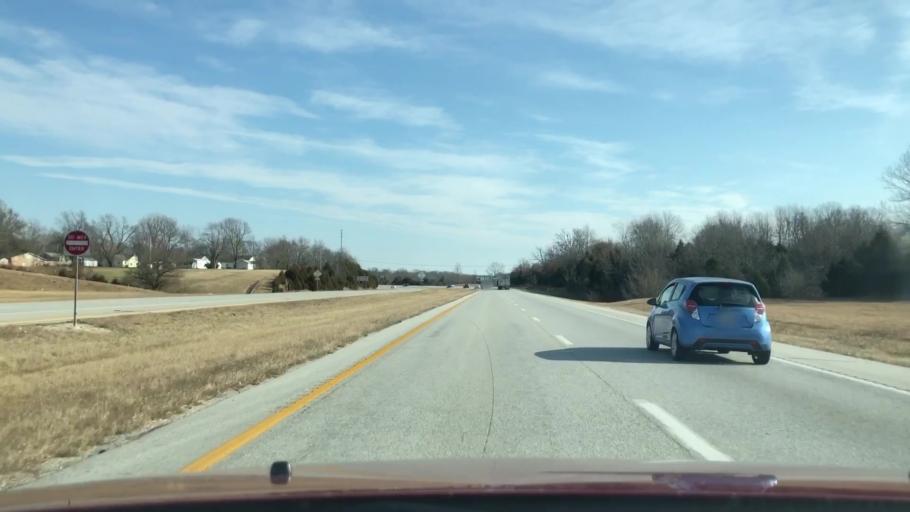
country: US
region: Missouri
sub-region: Webster County
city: Rogersville
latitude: 37.1518
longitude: -92.9431
